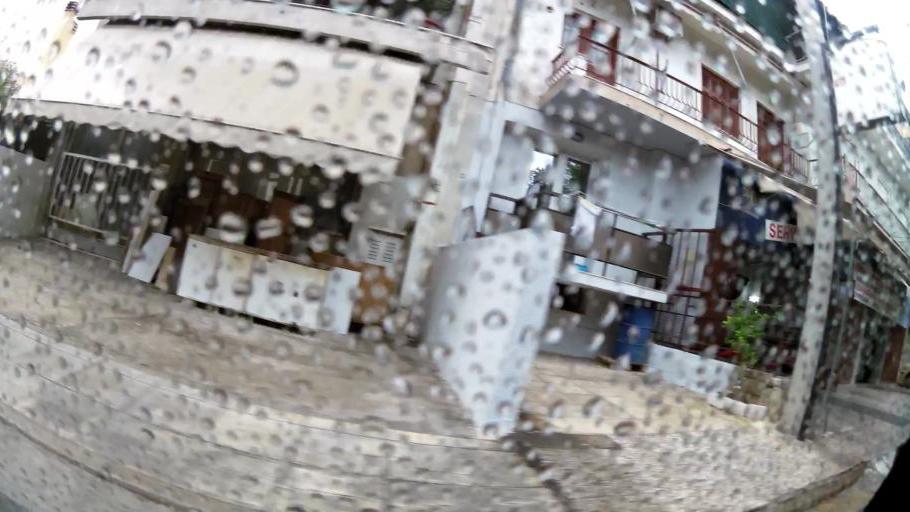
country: GR
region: Attica
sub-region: Nomarchia Athinas
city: Nea Chalkidona
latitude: 38.0196
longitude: 23.7232
